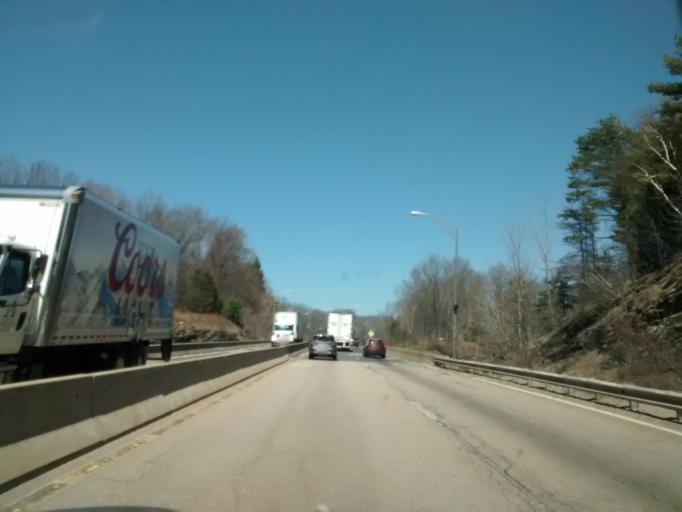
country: US
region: Massachusetts
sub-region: Worcester County
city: Auburn
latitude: 42.1918
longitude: -71.8533
